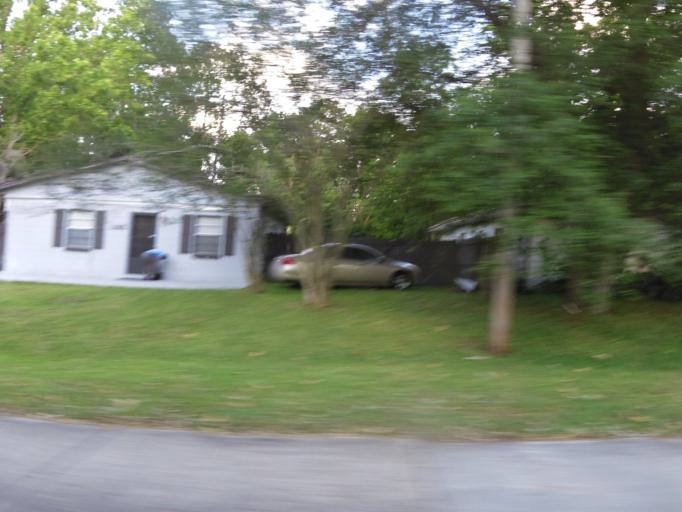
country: US
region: Florida
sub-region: Duval County
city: Jacksonville
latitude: 30.3038
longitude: -81.7393
